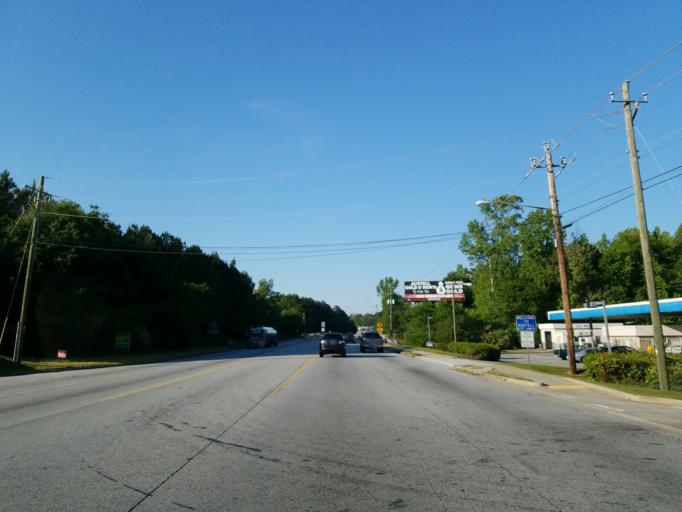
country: US
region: Georgia
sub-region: Cobb County
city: Austell
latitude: 33.7986
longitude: -84.6418
